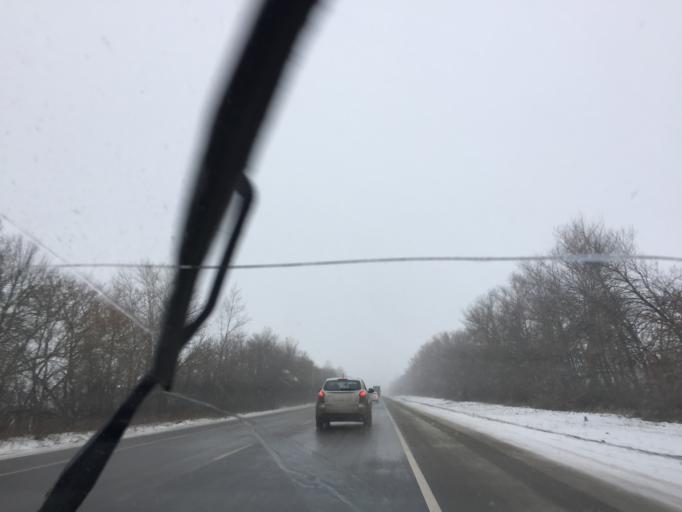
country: RU
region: Tula
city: Plavsk
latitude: 53.8013
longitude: 37.3804
